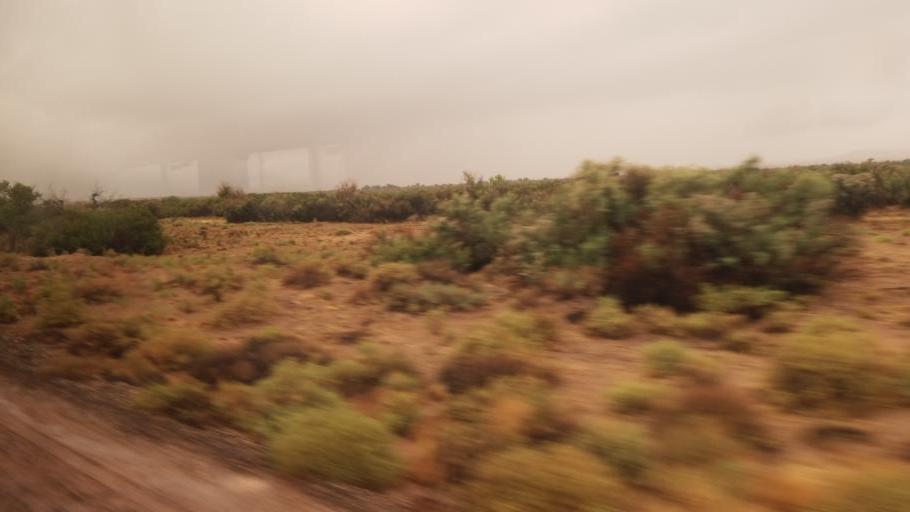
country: US
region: Arizona
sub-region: Navajo County
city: Joseph City
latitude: 34.9674
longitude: -110.4550
